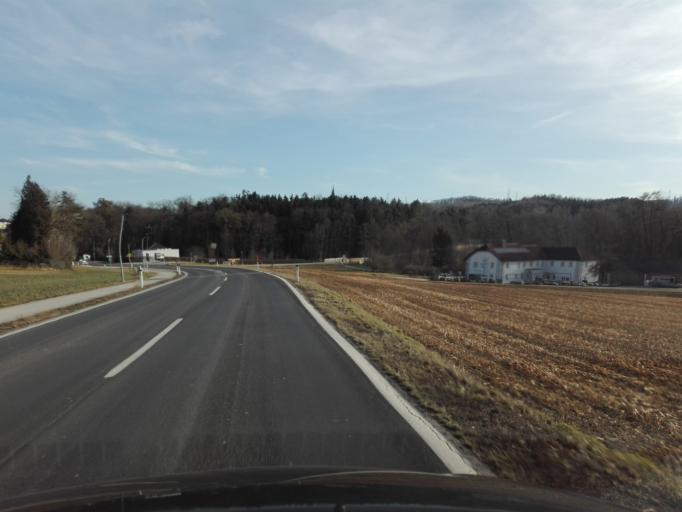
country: AT
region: Lower Austria
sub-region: Politischer Bezirk Amstetten
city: Amstetten
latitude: 48.1652
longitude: 14.8417
